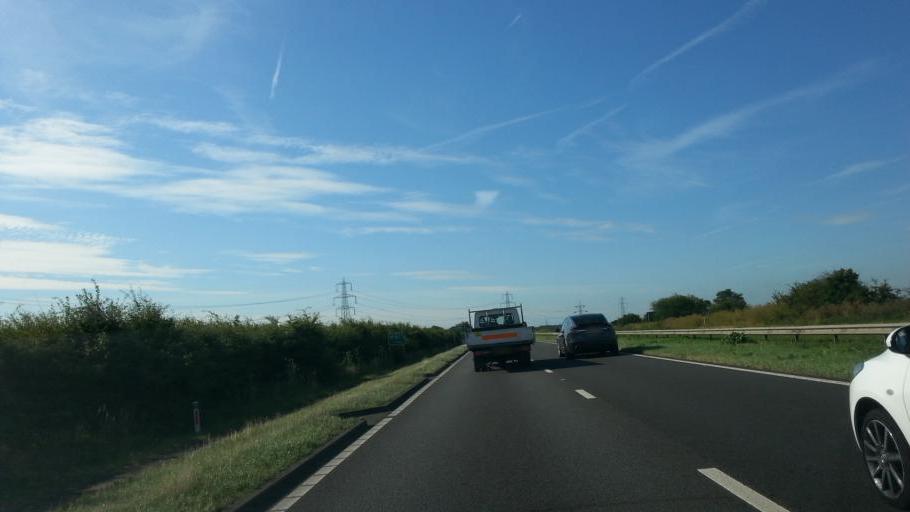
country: GB
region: England
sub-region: Lincolnshire
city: Long Bennington
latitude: 53.0226
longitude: -0.7676
